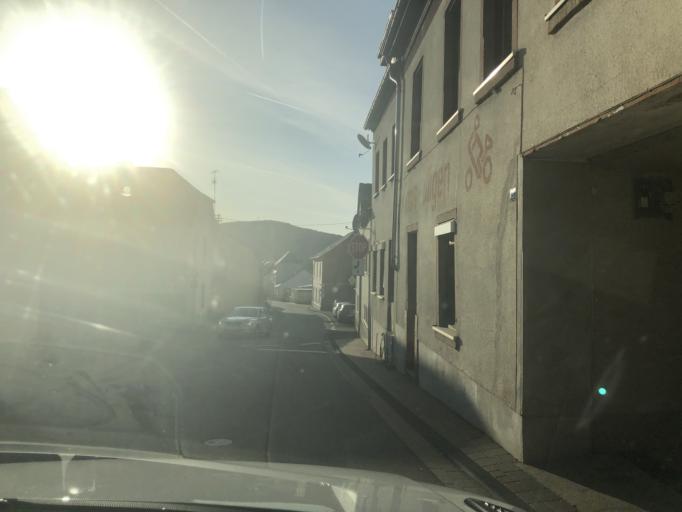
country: DE
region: Rheinland-Pfalz
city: Mertesdorf
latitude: 49.7729
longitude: 6.7366
